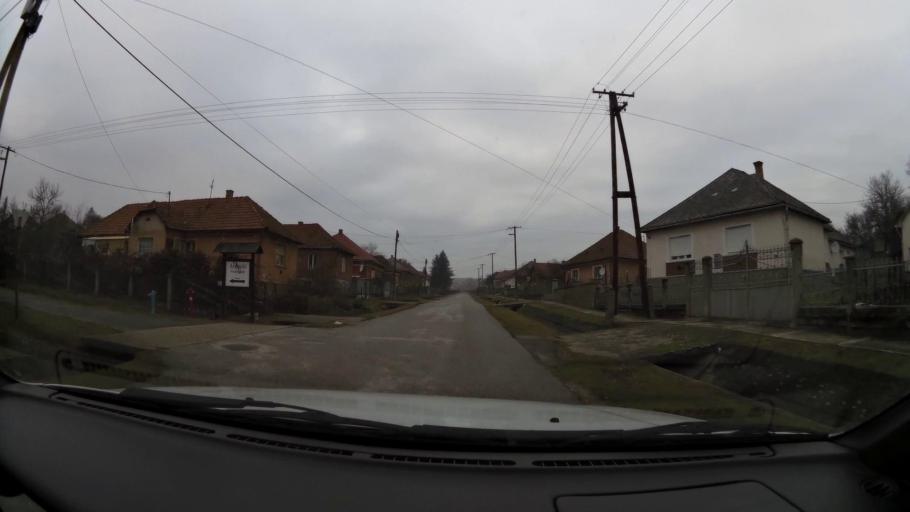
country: HU
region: Borsod-Abauj-Zemplen
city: Rudabanya
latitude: 48.4120
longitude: 20.6535
